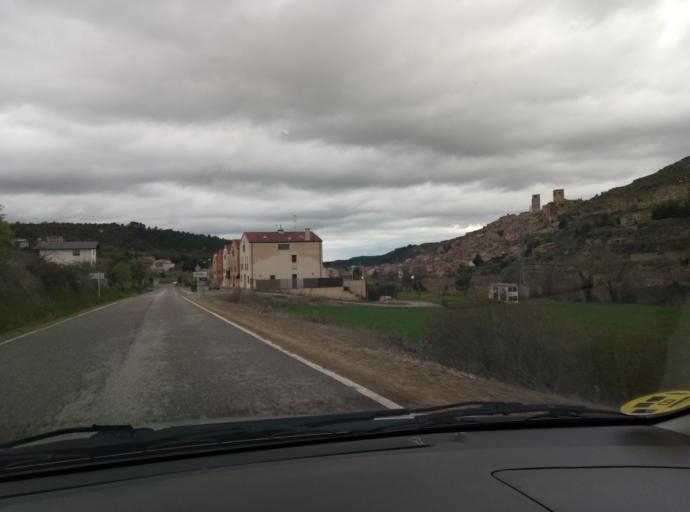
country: ES
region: Catalonia
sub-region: Provincia de Lleida
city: Guimera
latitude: 41.5625
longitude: 1.1920
